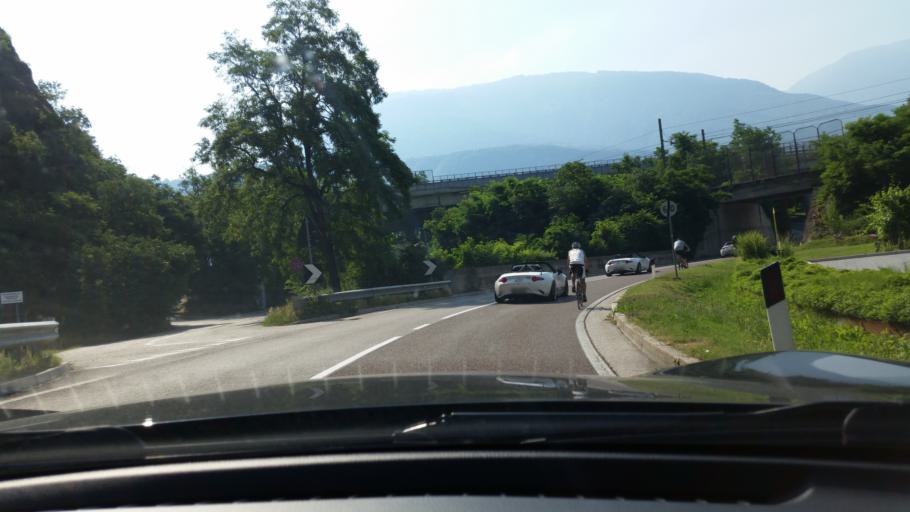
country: IT
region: Trentino-Alto Adige
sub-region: Bolzano
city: Ora
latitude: 46.3543
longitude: 11.2849
